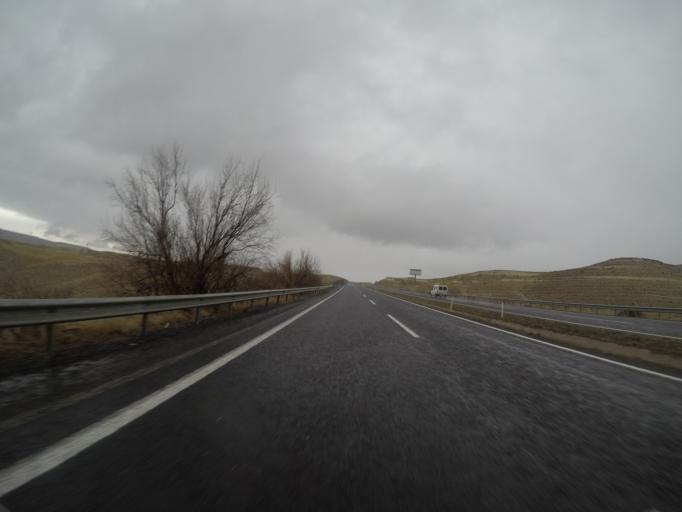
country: TR
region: Nevsehir
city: Urgub
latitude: 38.7397
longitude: 34.9985
